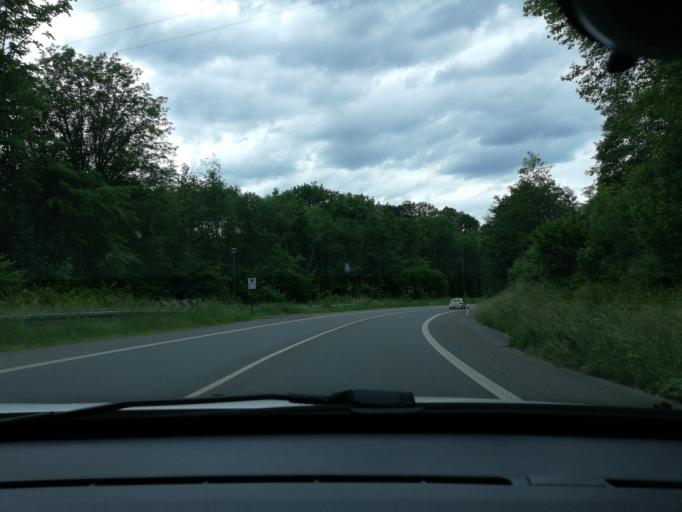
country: DE
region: North Rhine-Westphalia
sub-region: Regierungsbezirk Arnsberg
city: Hagen
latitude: 51.3113
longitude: 7.5267
